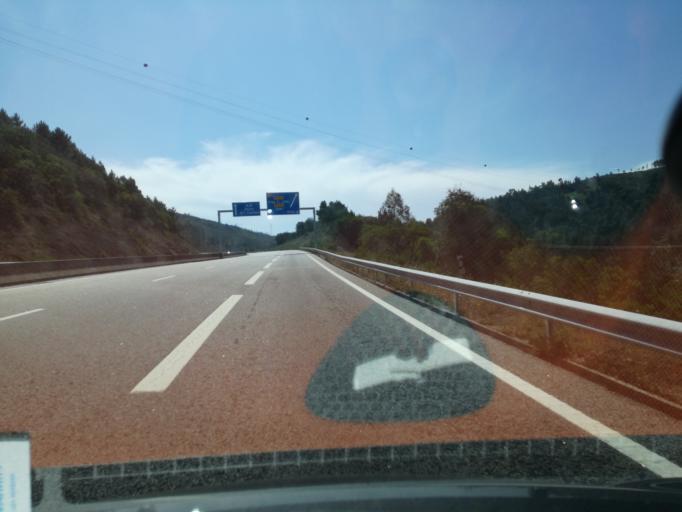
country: PT
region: Viana do Castelo
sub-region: Caminha
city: Vila Praia de Ancora
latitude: 41.8592
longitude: -8.7777
